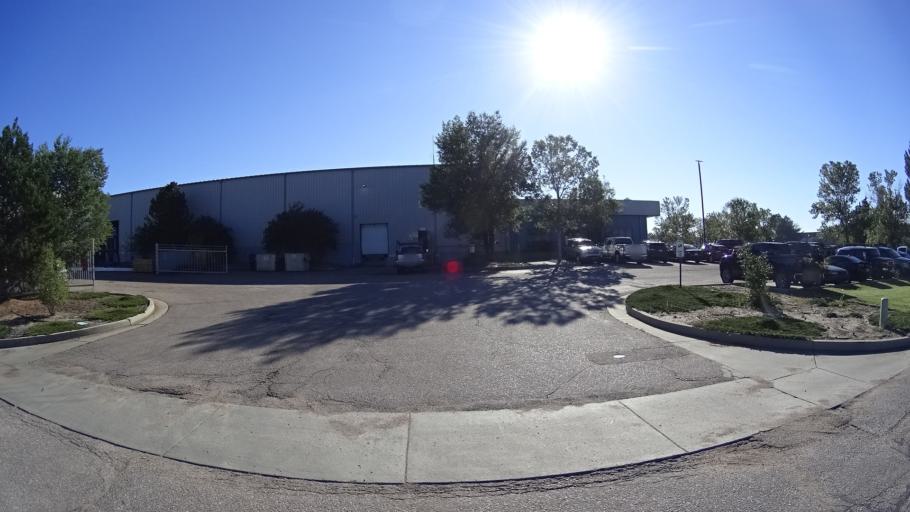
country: US
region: Colorado
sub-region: El Paso County
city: Cimarron Hills
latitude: 38.8151
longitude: -104.7253
